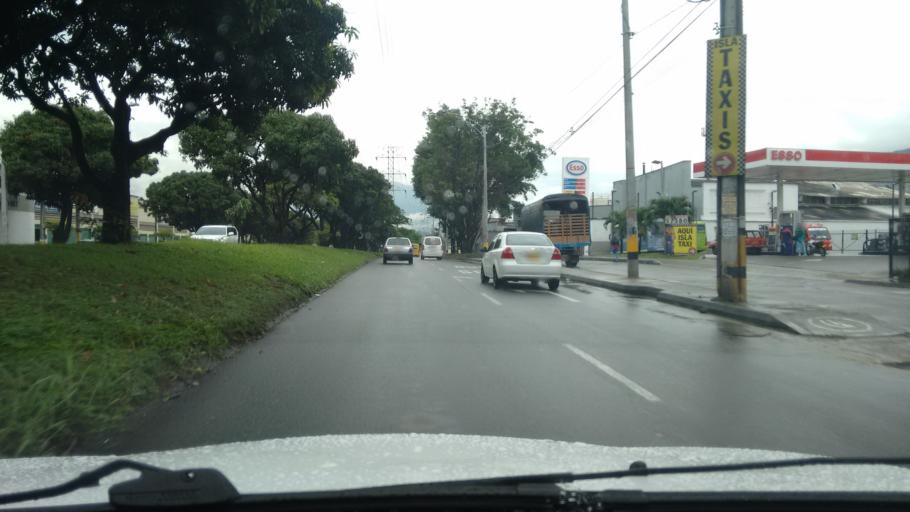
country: CO
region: Antioquia
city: Medellin
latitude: 6.2713
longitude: -75.5754
